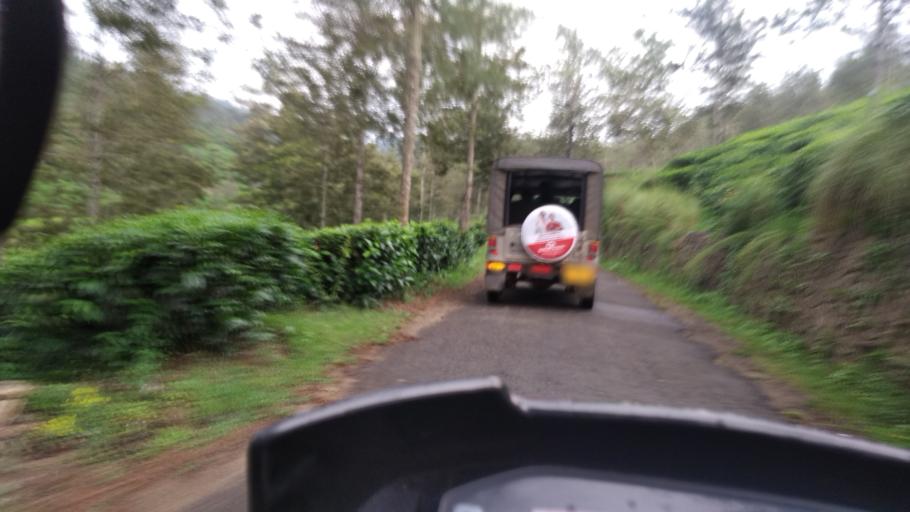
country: IN
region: Tamil Nadu
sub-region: Theni
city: Gudalur
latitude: 9.5578
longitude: 77.0719
